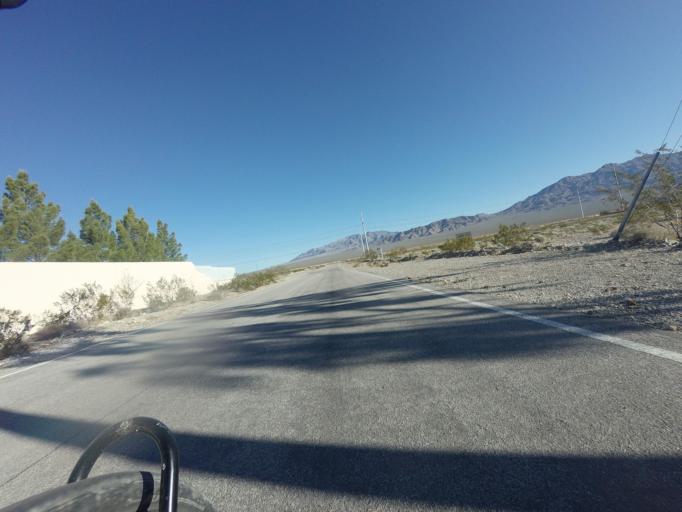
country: US
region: Nevada
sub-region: Clark County
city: North Las Vegas
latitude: 36.3330
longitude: -115.2829
